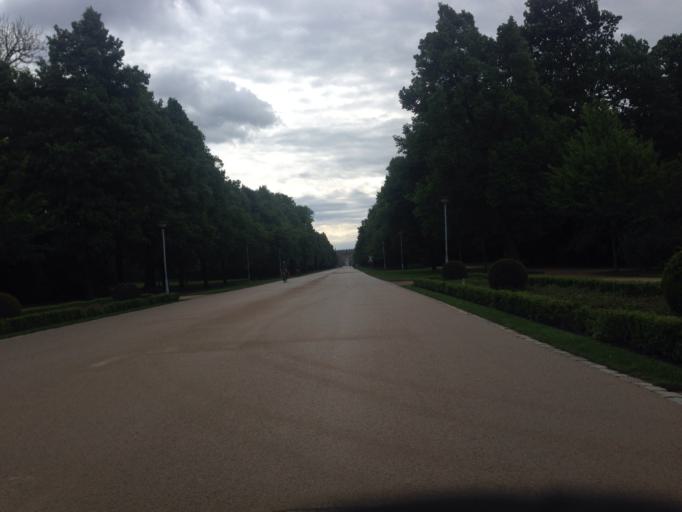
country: DE
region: Saxony
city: Dresden
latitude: 51.0423
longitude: 13.7517
